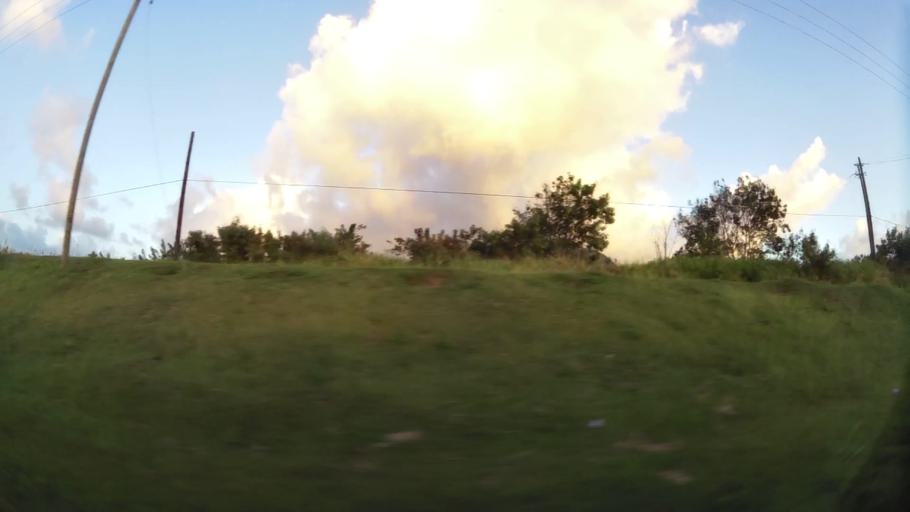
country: KN
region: Saint Anne Sandy Point
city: Sandy Point Town
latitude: 17.3742
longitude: -62.8531
